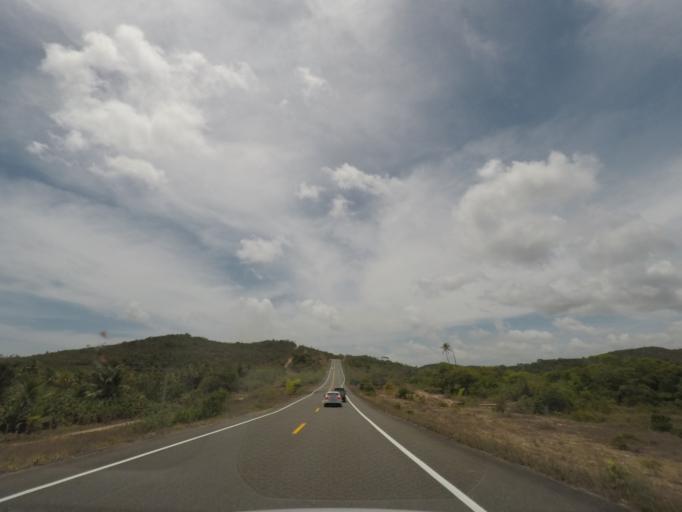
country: BR
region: Bahia
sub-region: Conde
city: Conde
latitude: -11.7270
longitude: -37.5786
